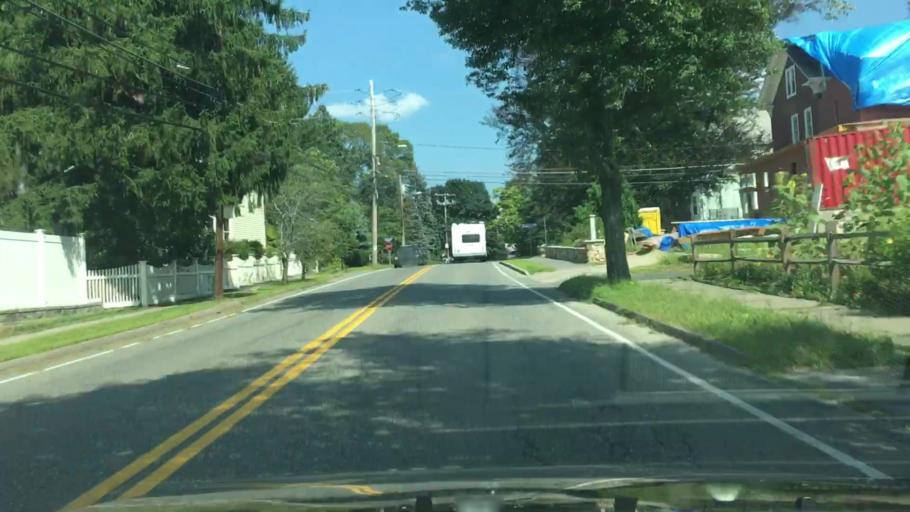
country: US
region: Massachusetts
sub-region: Middlesex County
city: Holliston
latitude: 42.2007
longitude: -71.4214
